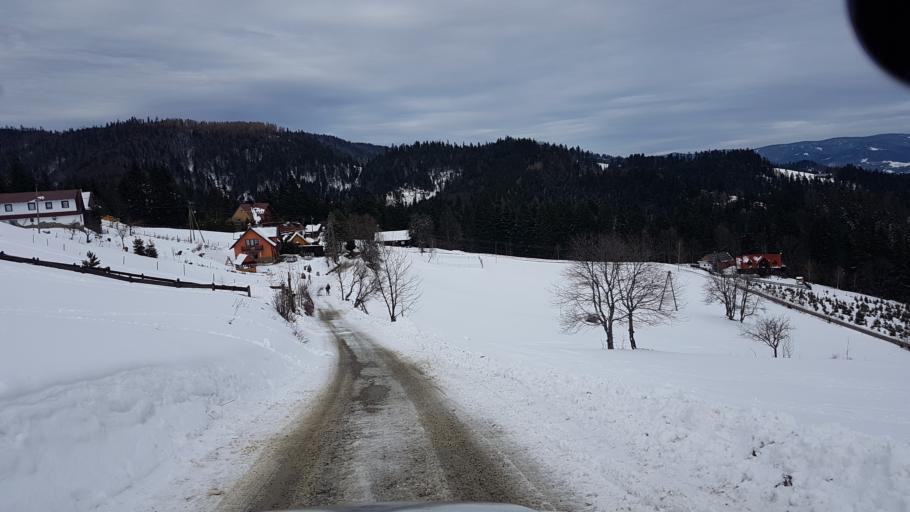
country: PL
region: Lesser Poland Voivodeship
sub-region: Powiat nowosadecki
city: Rytro
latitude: 49.4194
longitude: 20.6232
